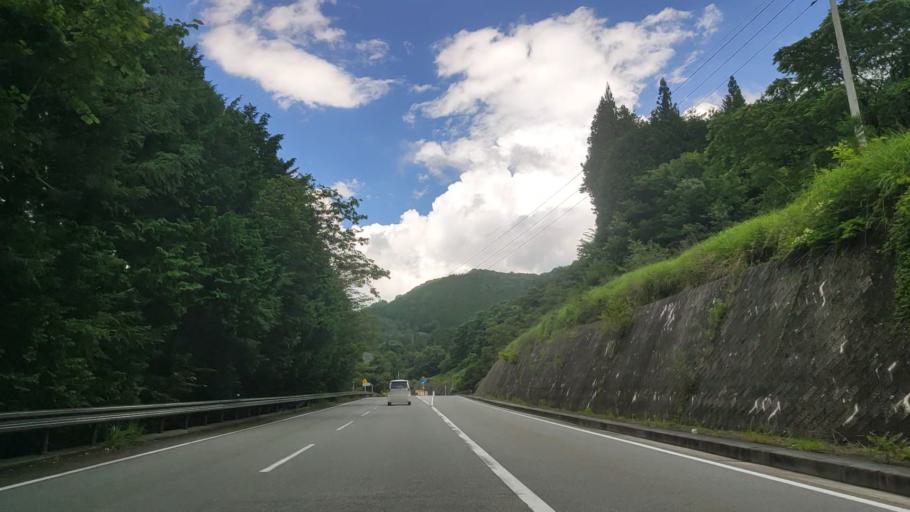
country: JP
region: Yamanashi
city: Enzan
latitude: 35.8133
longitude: 138.7538
